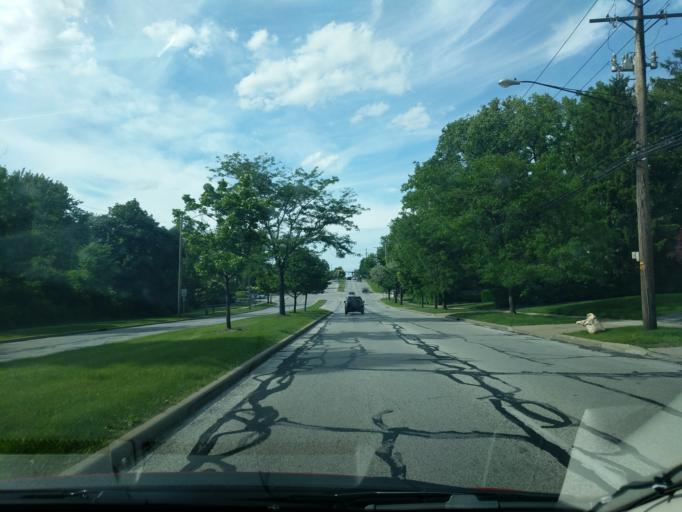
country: US
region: Ohio
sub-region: Cuyahoga County
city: Shaker Heights
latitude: 41.4826
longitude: -81.5362
